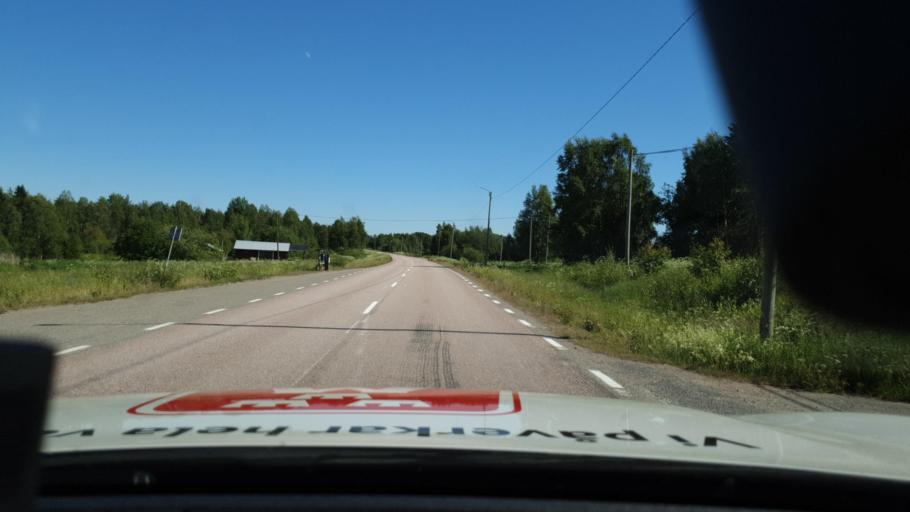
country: SE
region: Norrbotten
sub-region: Lulea Kommun
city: Ranea
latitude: 65.9323
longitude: 22.4168
